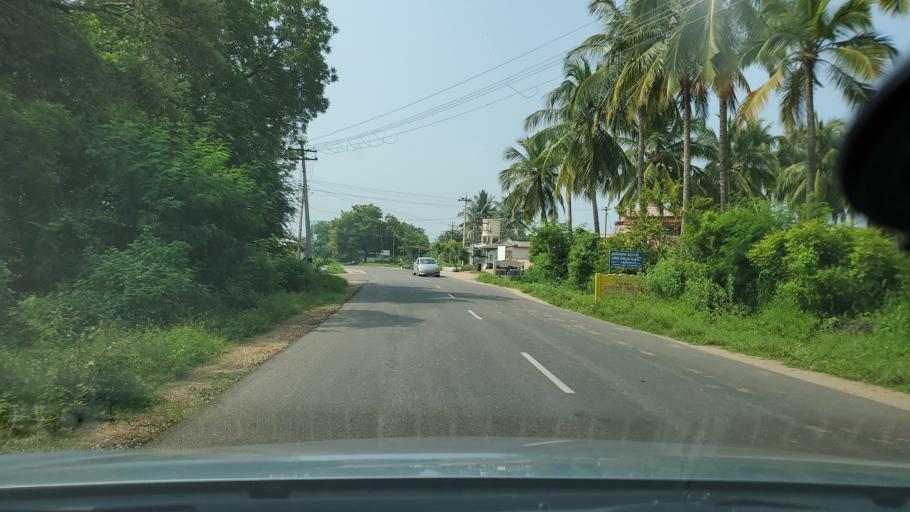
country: IN
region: Tamil Nadu
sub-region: Erode
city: Chennimalai
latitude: 11.1962
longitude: 77.6264
